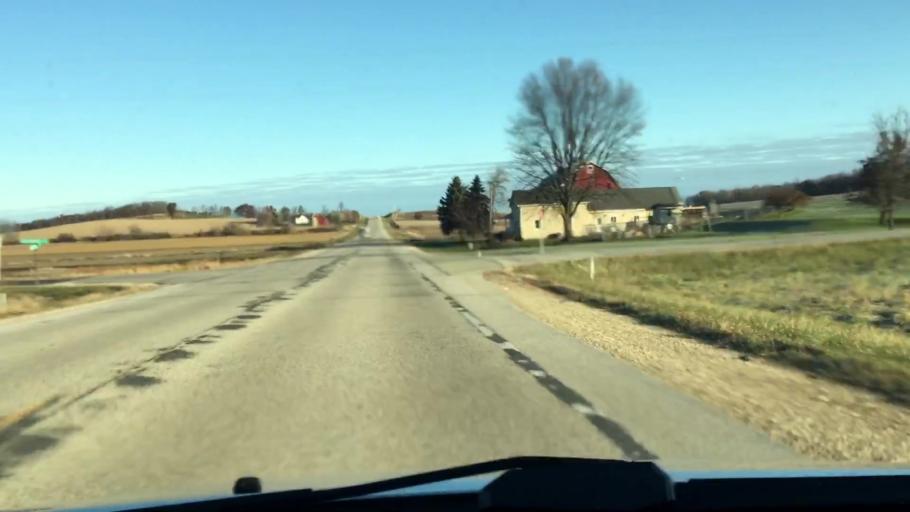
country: US
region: Wisconsin
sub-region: Dodge County
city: Theresa
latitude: 43.4710
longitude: -88.4500
